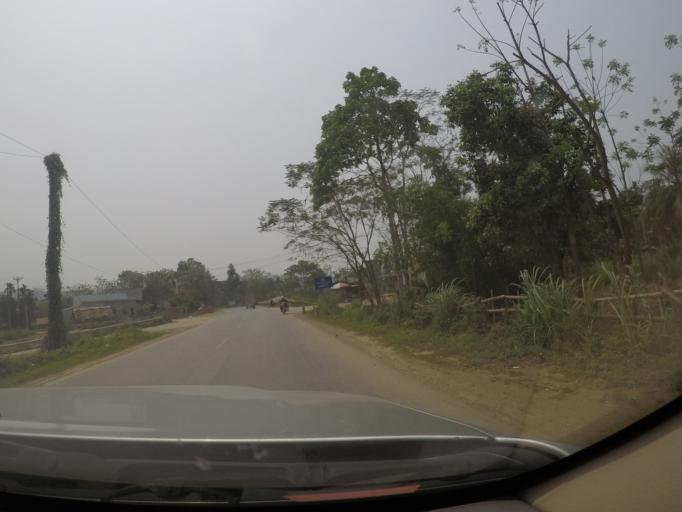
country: VN
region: Thanh Hoa
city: Thi Tran Thuong Xuan
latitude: 19.9685
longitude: 105.3993
